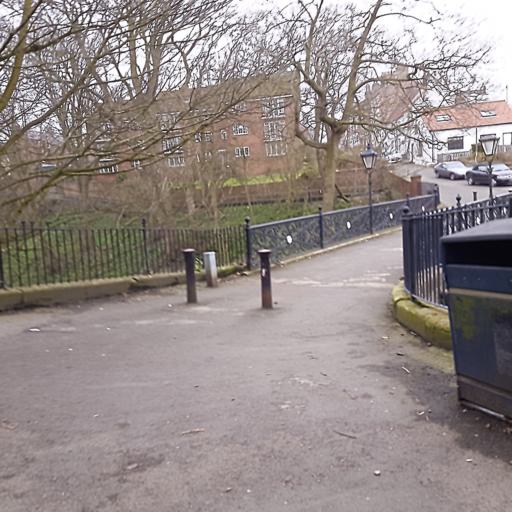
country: GB
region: England
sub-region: North Yorkshire
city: Filey
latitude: 54.2134
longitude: -0.2886
